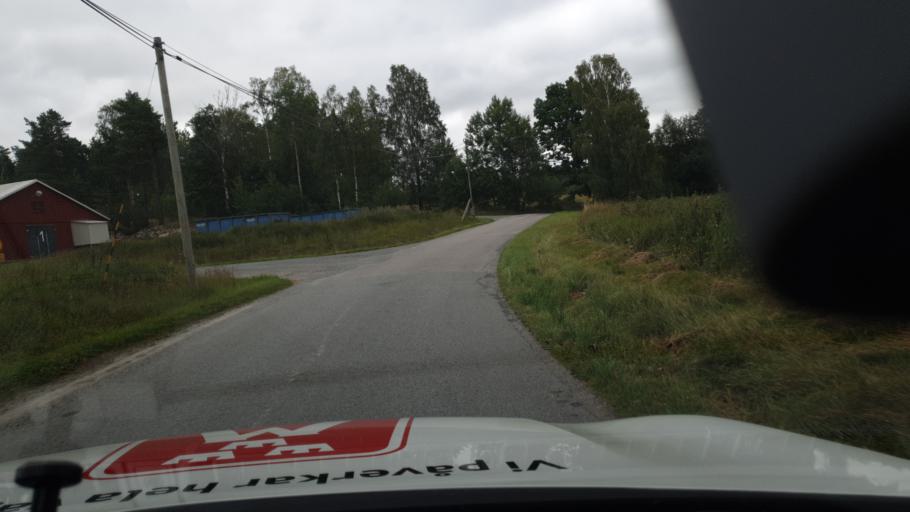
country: SE
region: Soedermanland
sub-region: Strangnas Kommun
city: Akers Styckebruk
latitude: 59.1836
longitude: 17.1482
